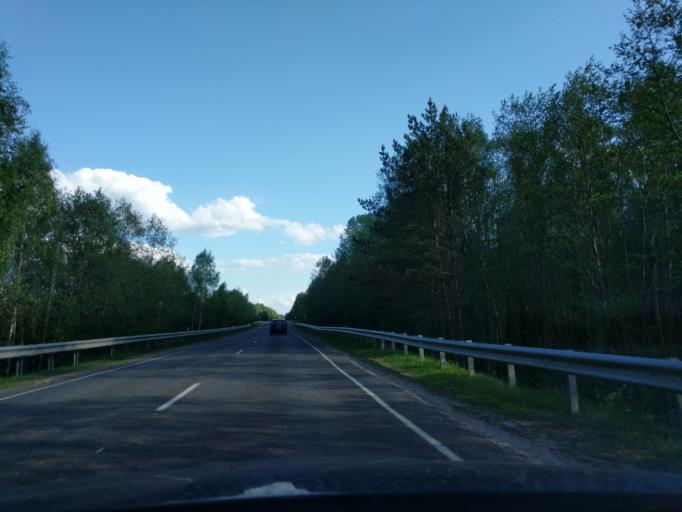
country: BY
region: Minsk
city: Kryvichy
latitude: 54.6093
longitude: 27.1795
